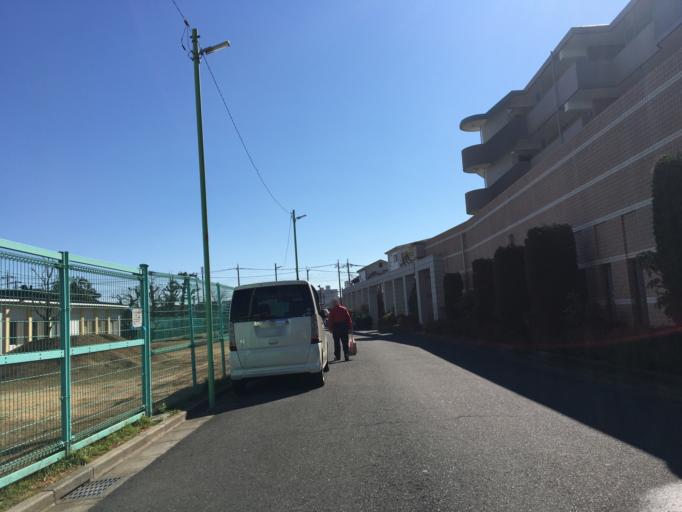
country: JP
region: Saitama
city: Shiki
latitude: 35.8099
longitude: 139.5696
